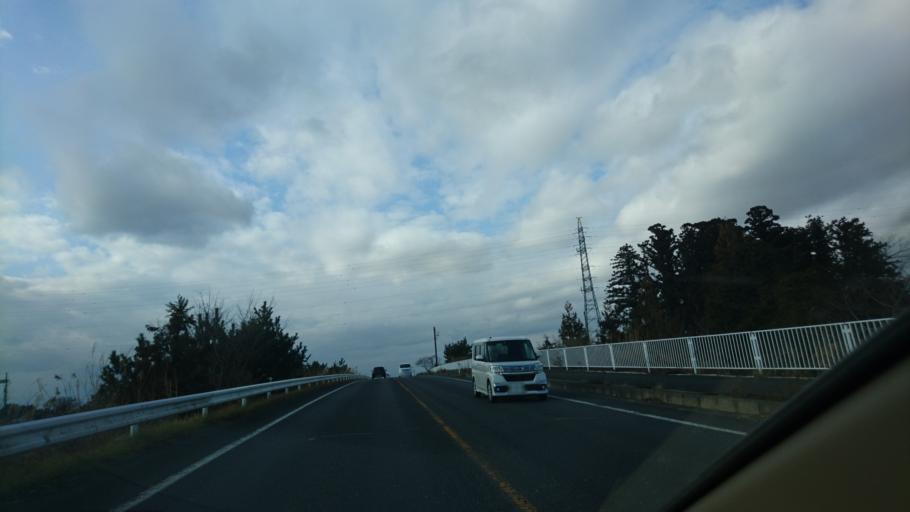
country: JP
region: Miyagi
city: Kogota
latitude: 38.5537
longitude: 141.0466
